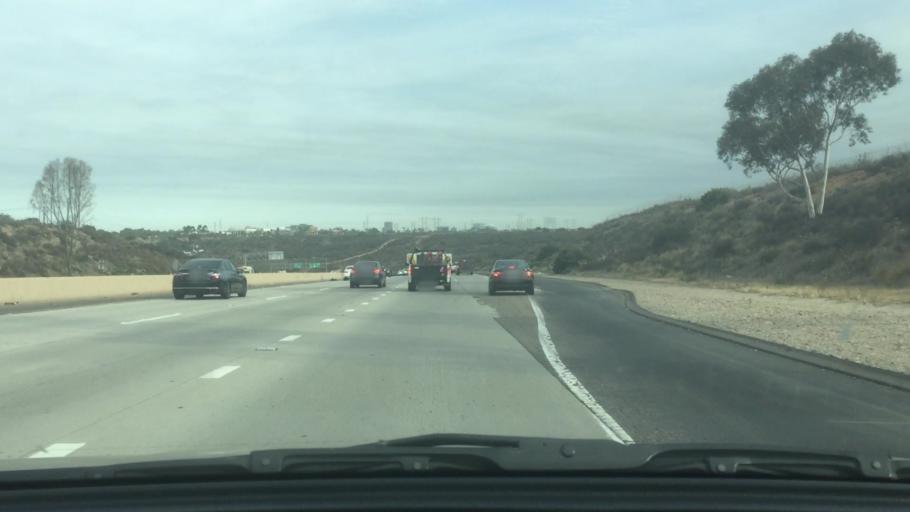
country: US
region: California
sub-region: San Diego County
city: La Jolla
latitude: 32.8426
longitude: -117.1673
